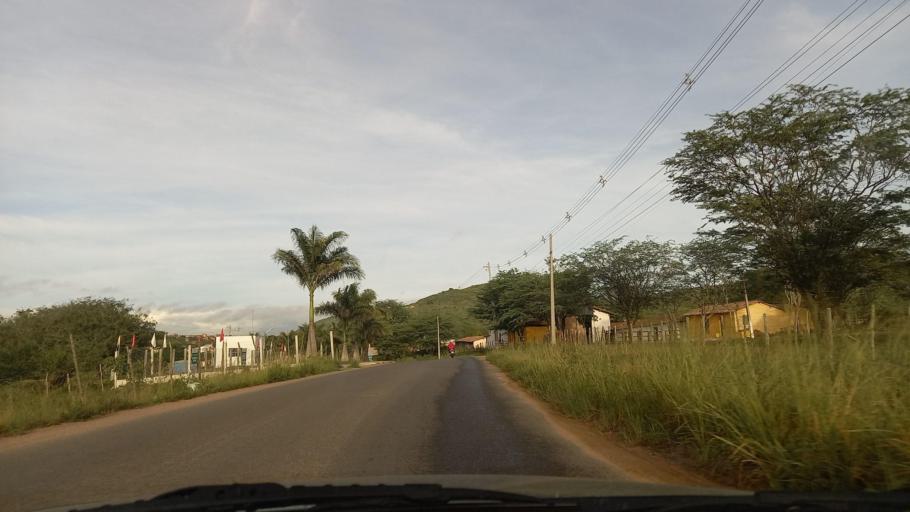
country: BR
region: Pernambuco
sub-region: Bezerros
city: Bezerros
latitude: -8.2173
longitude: -35.7460
